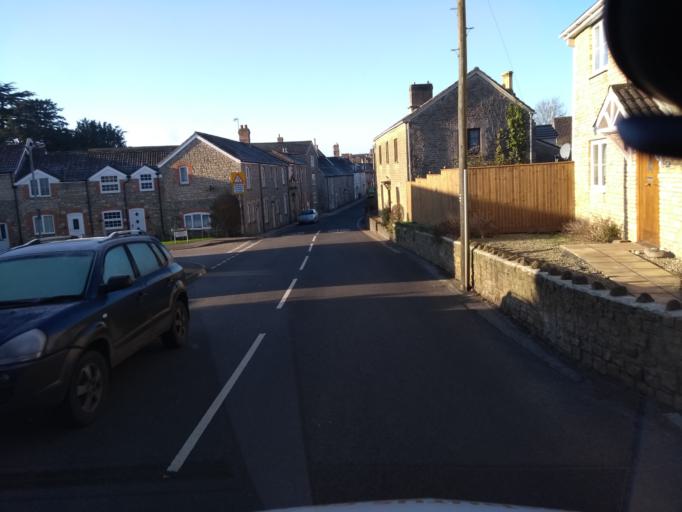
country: GB
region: England
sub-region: Somerset
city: Bruton
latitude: 51.1137
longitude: -2.4506
